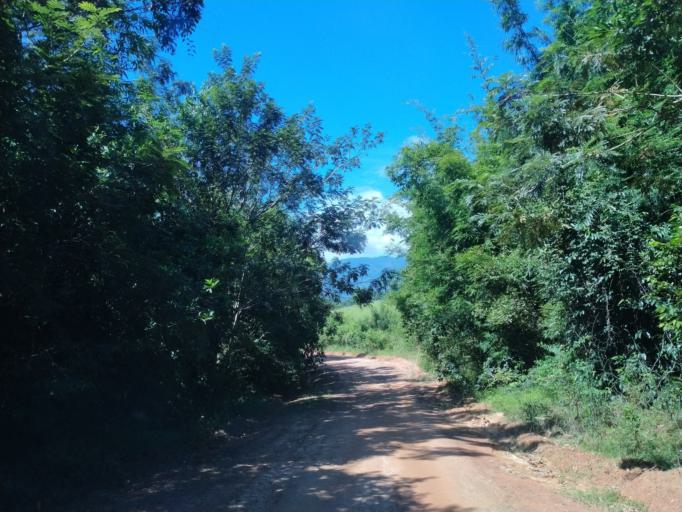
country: LA
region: Vientiane
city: Muang Phon-Hong
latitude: 18.6218
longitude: 102.8731
